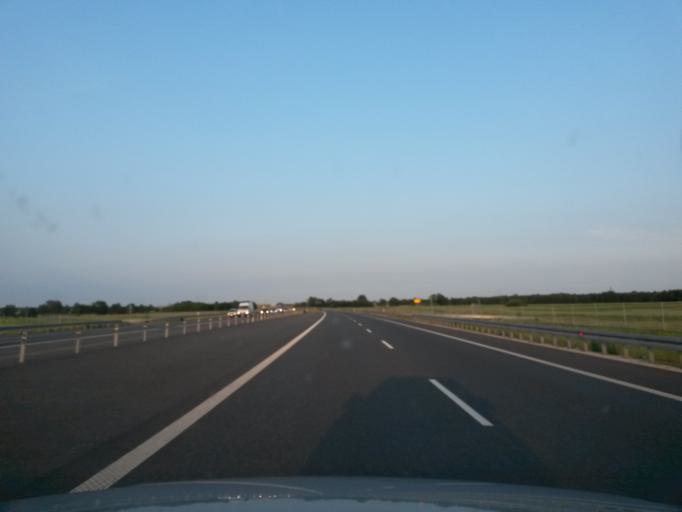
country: PL
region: Lodz Voivodeship
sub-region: Powiat wieruszowski
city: Sokolniki
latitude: 51.3199
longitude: 18.3494
